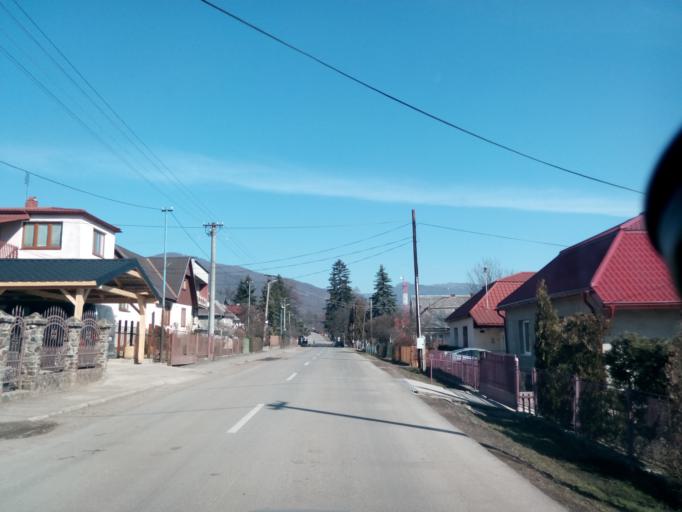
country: SK
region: Kosicky
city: Sobrance
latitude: 48.8469
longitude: 22.1835
